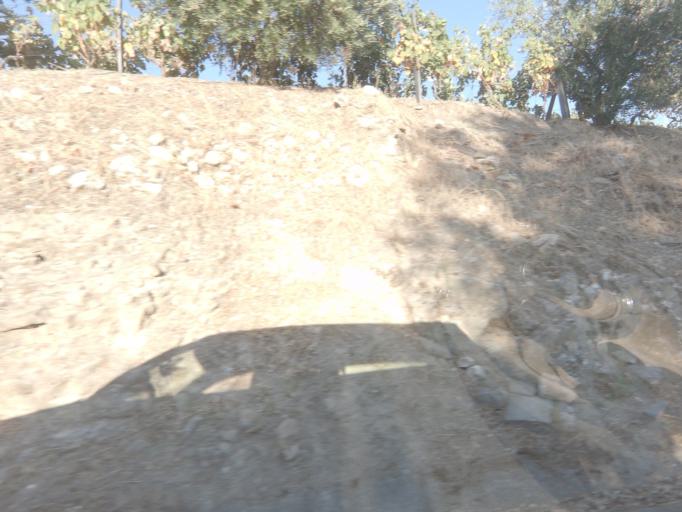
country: PT
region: Vila Real
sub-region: Peso da Regua
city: Godim
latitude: 41.1689
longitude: -7.8312
